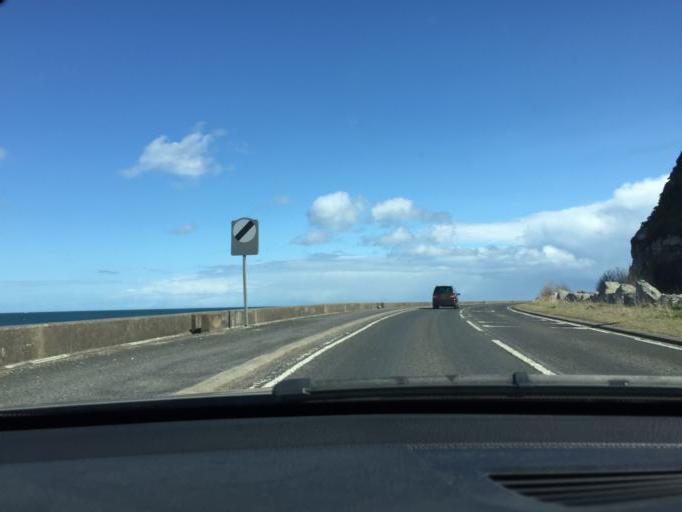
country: GB
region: Northern Ireland
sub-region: Larne District
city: Carnlough
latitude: 54.9705
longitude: -5.9461
